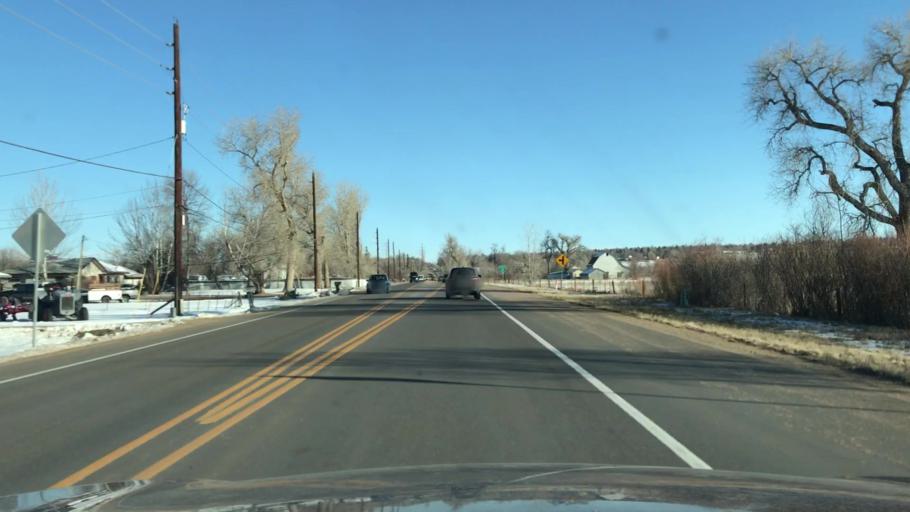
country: US
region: Colorado
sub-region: Boulder County
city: Gunbarrel
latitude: 40.0434
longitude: -105.1784
